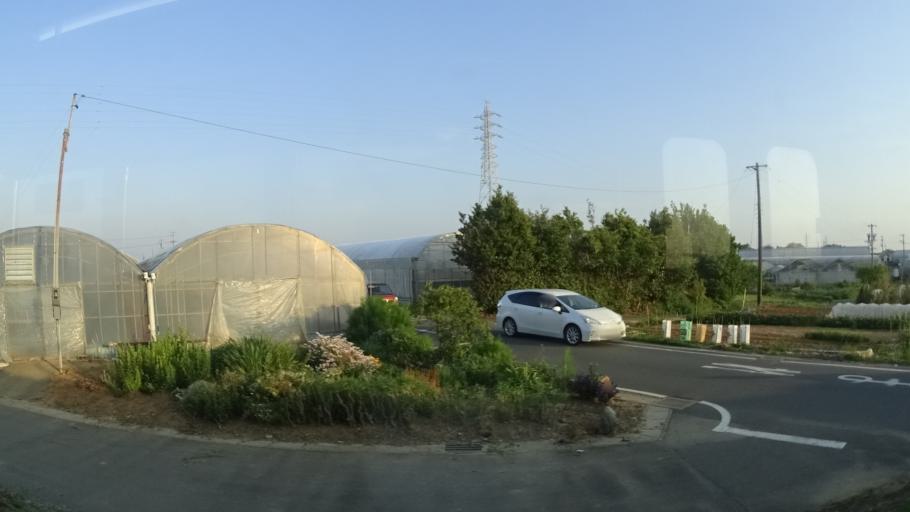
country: JP
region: Aichi
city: Toyohashi
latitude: 34.6941
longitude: 137.3477
